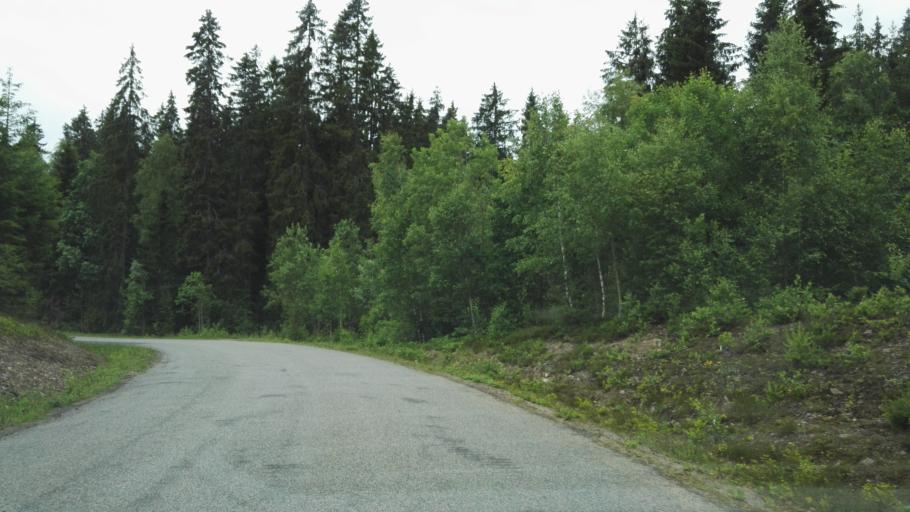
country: SE
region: Joenkoeping
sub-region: Vetlanda Kommun
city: Landsbro
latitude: 57.2251
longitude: 14.8201
